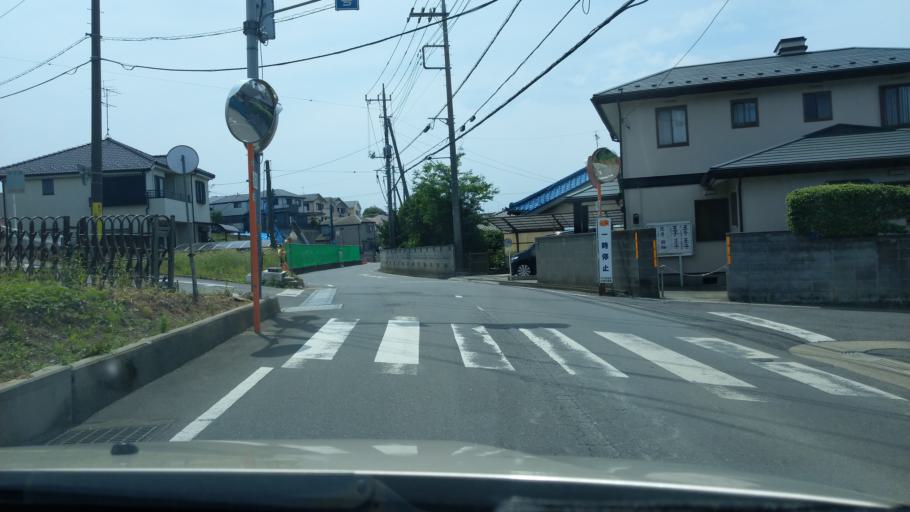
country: JP
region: Saitama
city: Saitama
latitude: 35.9038
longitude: 139.6505
